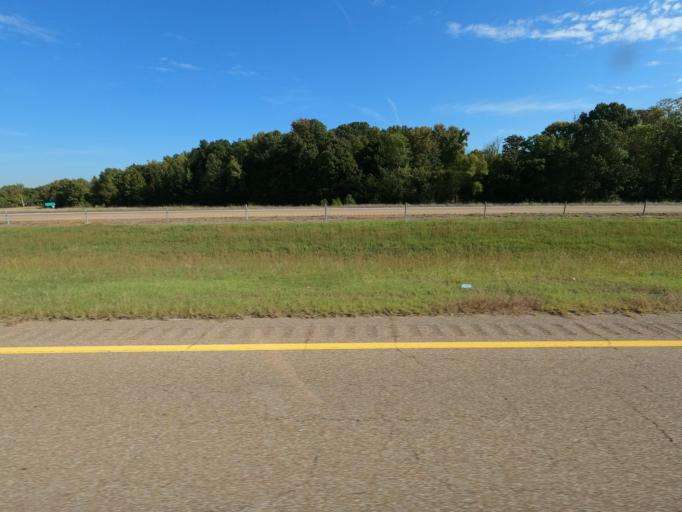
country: US
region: Tennessee
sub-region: Shelby County
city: Millington
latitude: 35.3176
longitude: -89.8710
